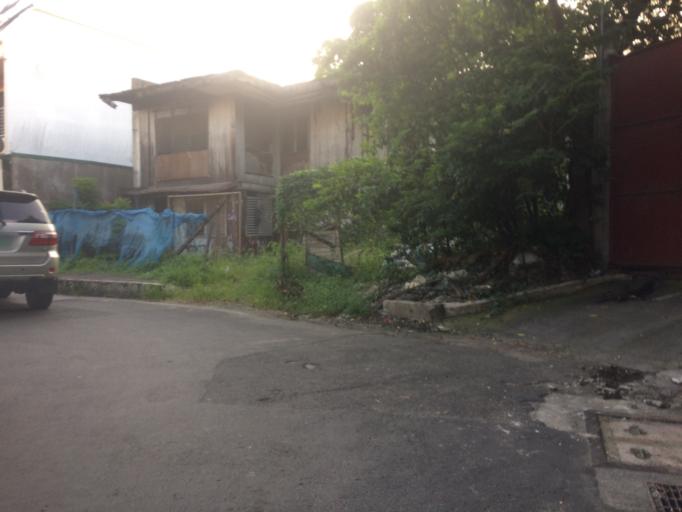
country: PH
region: Calabarzon
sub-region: Province of Rizal
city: Cainta
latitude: 14.5923
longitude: 121.1041
